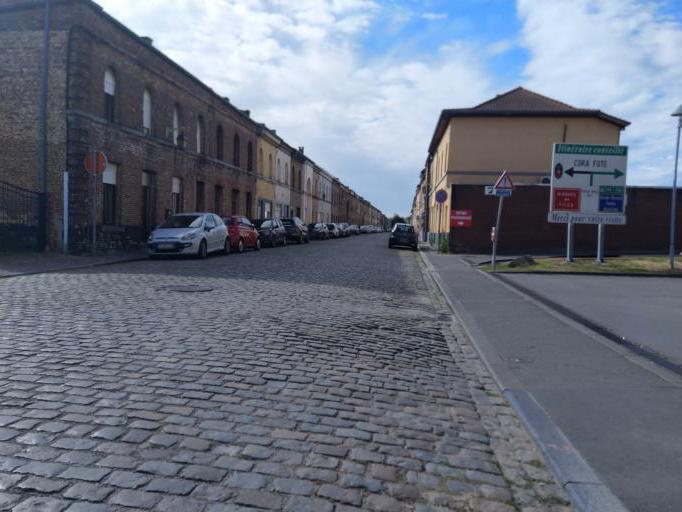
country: BE
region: Wallonia
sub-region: Province du Hainaut
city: Saint-Ghislain
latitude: 50.4384
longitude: 3.8403
